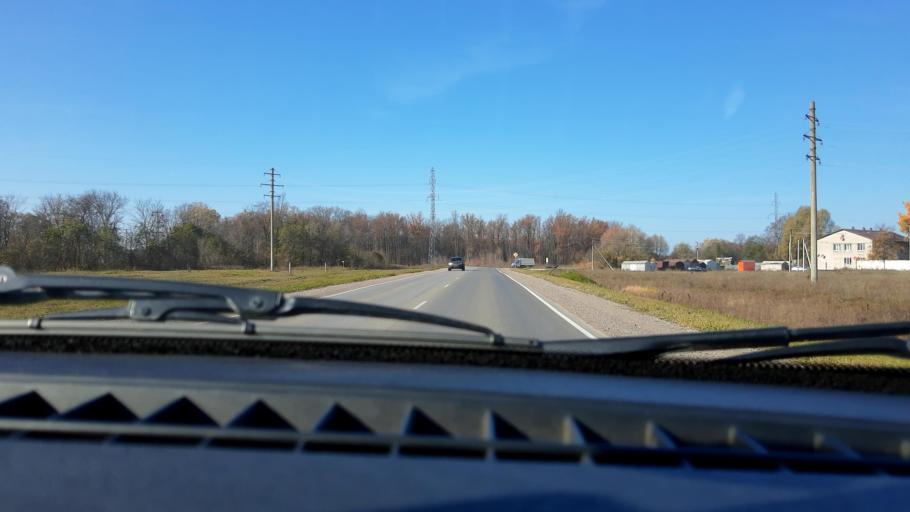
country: RU
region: Bashkortostan
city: Mikhaylovka
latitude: 54.8038
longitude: 55.8268
